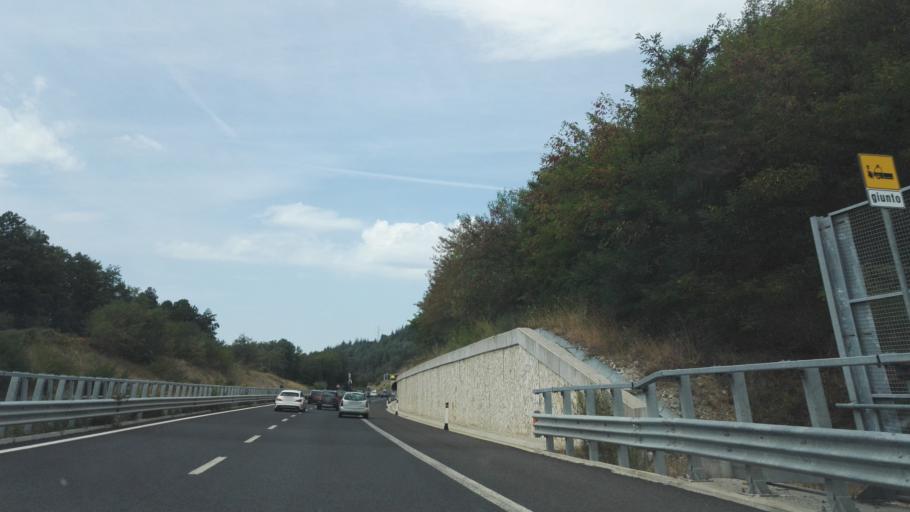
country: IT
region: Basilicate
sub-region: Provincia di Potenza
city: Nemoli
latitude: 40.0946
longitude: 15.8163
